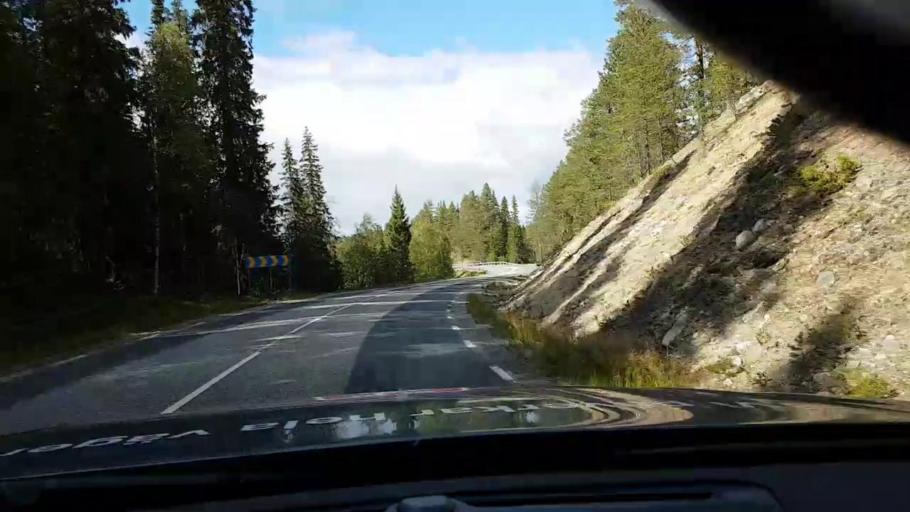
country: SE
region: Vaesterbotten
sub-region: Asele Kommun
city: Asele
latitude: 63.8373
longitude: 17.4351
